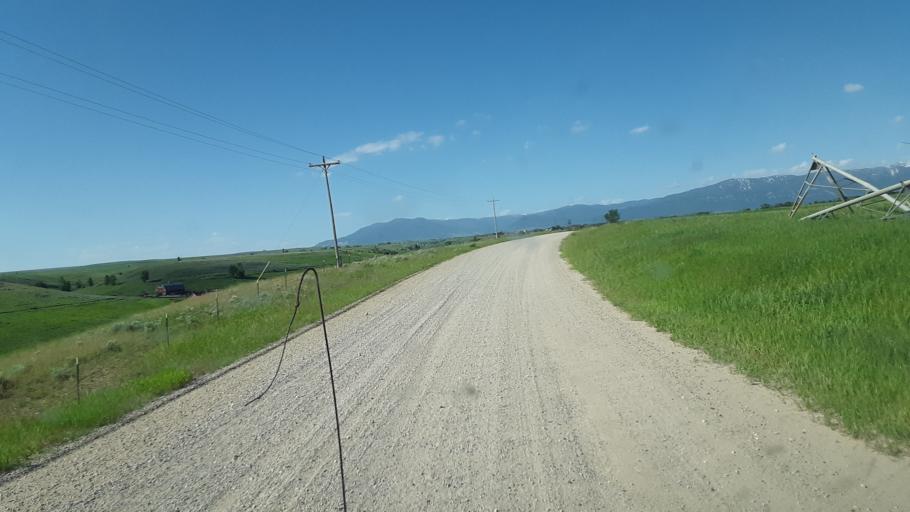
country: US
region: Montana
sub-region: Carbon County
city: Red Lodge
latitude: 45.3341
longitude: -109.1639
